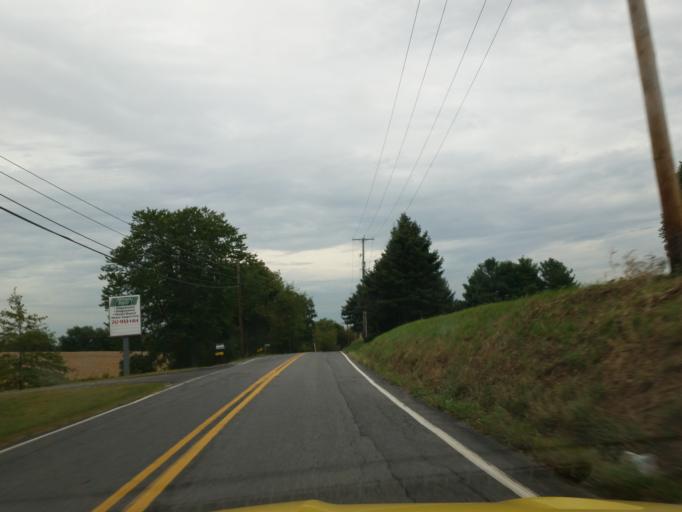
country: US
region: Pennsylvania
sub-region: Lebanon County
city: Fredericksburg
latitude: 40.4488
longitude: -76.3600
